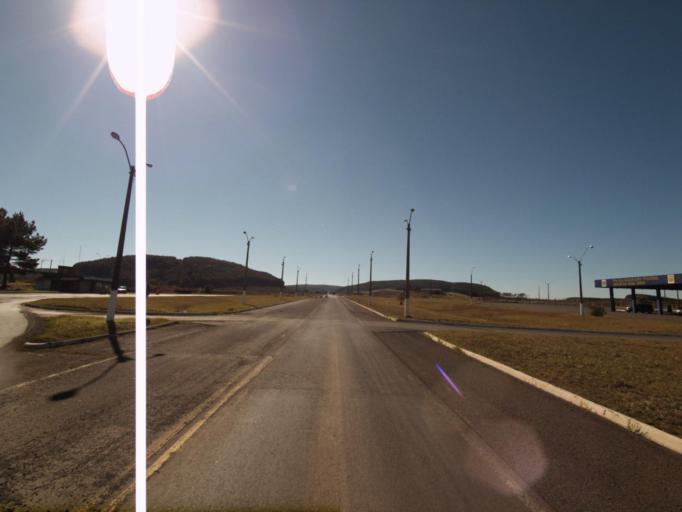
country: BR
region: Parana
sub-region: Palmas
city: Palmas
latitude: -26.6811
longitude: -51.5597
